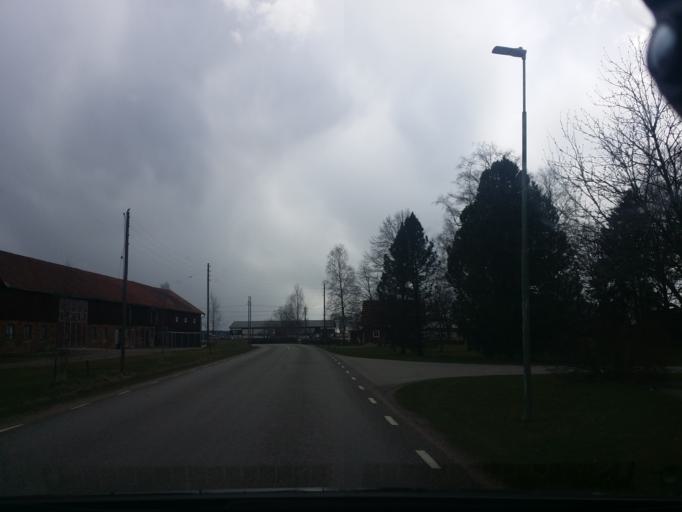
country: SE
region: Vaestmanland
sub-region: Sala Kommun
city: Sala
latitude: 59.9147
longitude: 16.6284
